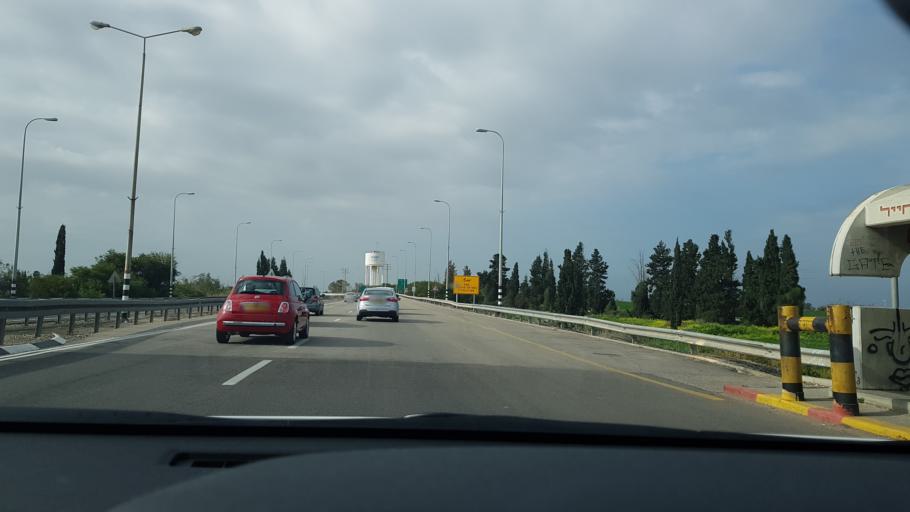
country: IL
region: Southern District
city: Ashqelon
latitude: 31.6582
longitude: 34.6020
